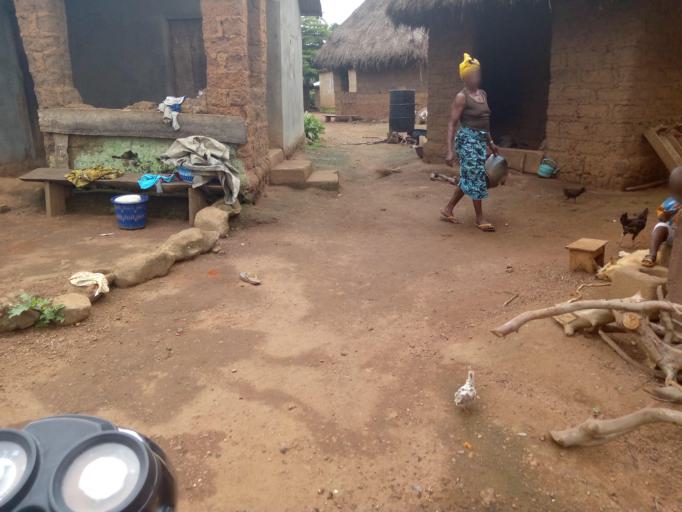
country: SL
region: Eastern Province
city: Buedu
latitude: 8.4807
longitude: -10.3270
